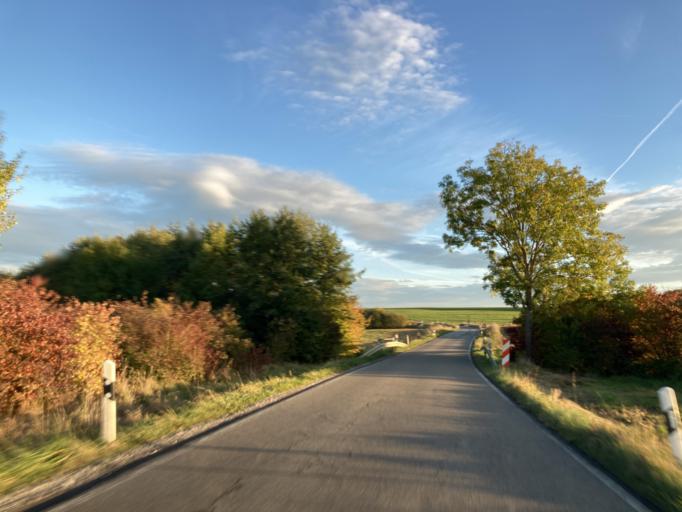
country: DE
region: Baden-Wuerttemberg
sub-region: Regierungsbezirk Stuttgart
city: Motzingen
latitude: 48.4974
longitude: 8.7751
